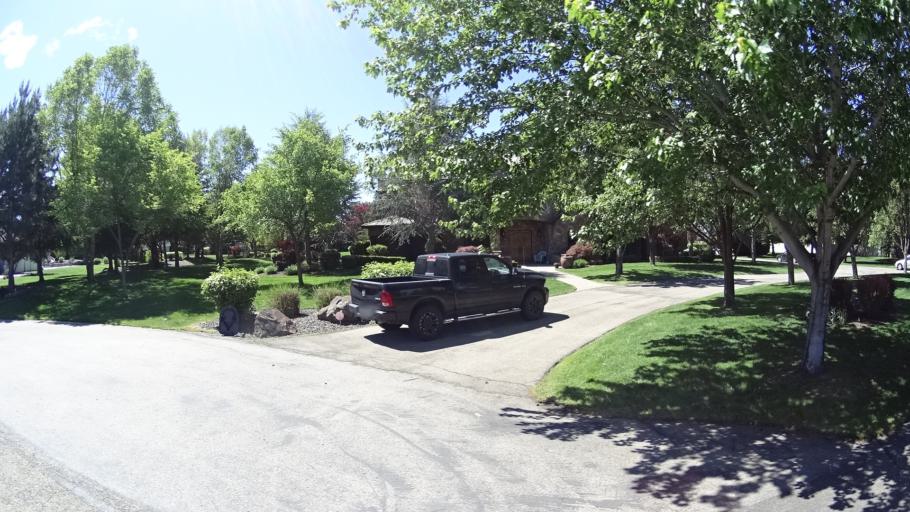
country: US
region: Idaho
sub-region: Ada County
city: Eagle
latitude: 43.6673
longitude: -116.3849
